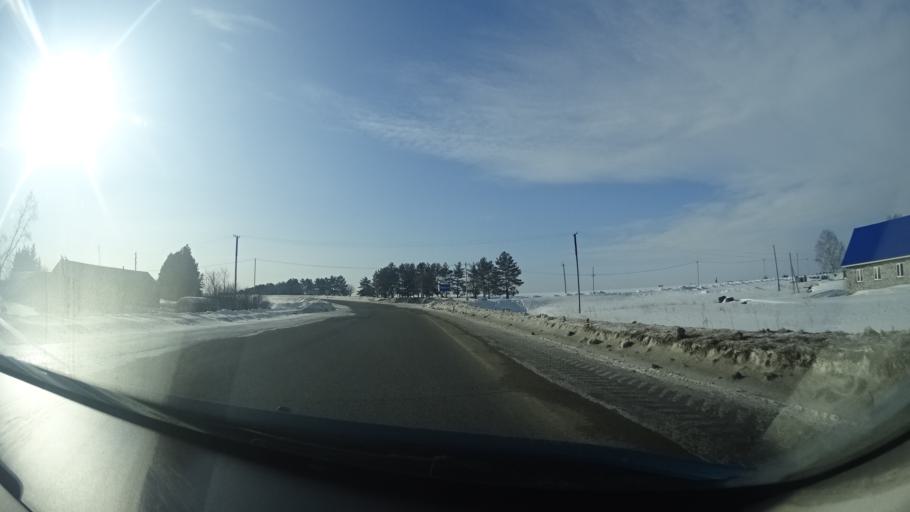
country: RU
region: Perm
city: Kuyeda
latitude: 56.4716
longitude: 55.5886
